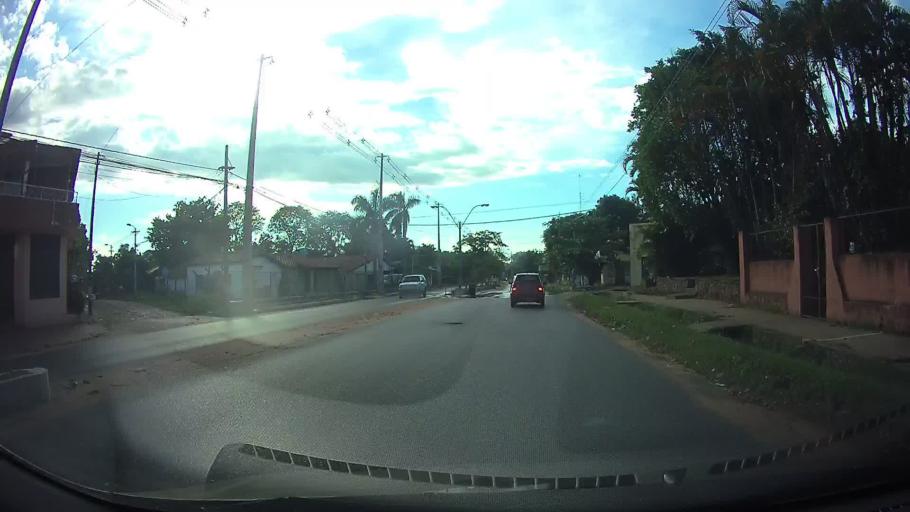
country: PY
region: Central
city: San Antonio
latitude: -25.4195
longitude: -57.5683
